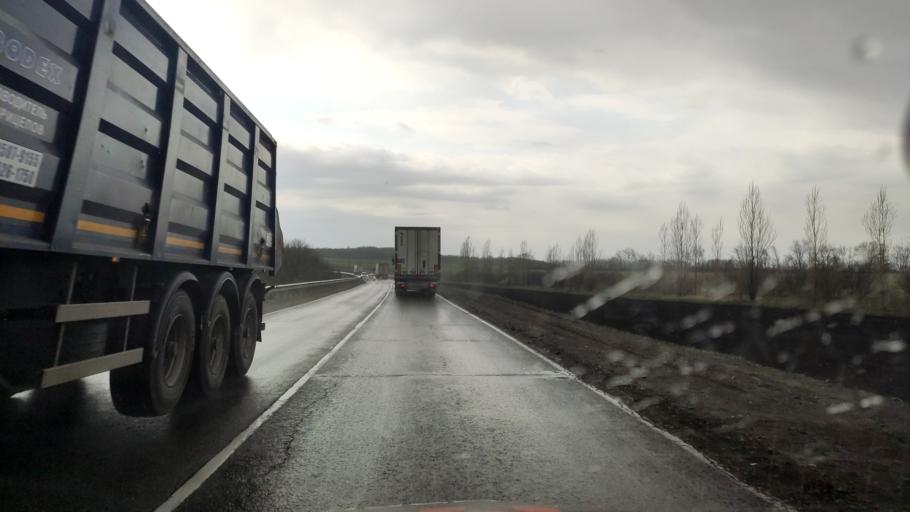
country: RU
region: Voronezj
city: Nizhnedevitsk
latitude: 51.5763
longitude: 38.3197
